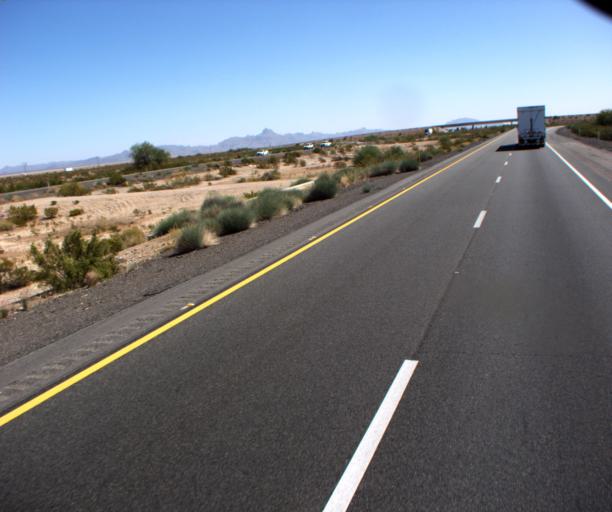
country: US
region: Arizona
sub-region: La Paz County
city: Salome
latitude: 33.5697
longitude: -113.3593
